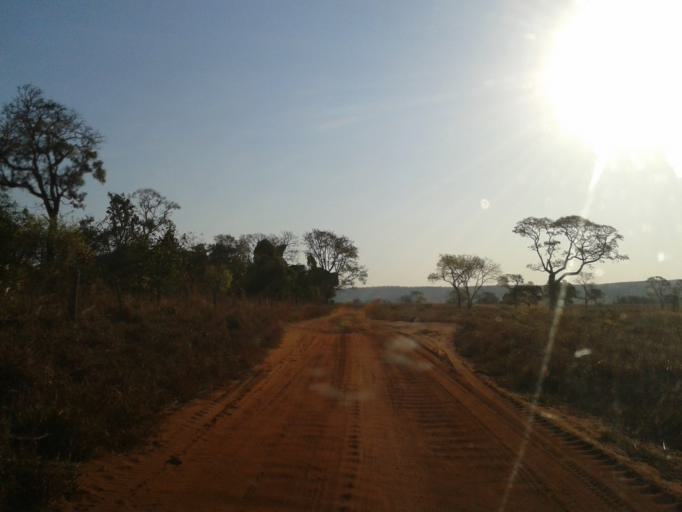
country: BR
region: Minas Gerais
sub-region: Ituiutaba
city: Ituiutaba
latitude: -19.2431
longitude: -49.5942
